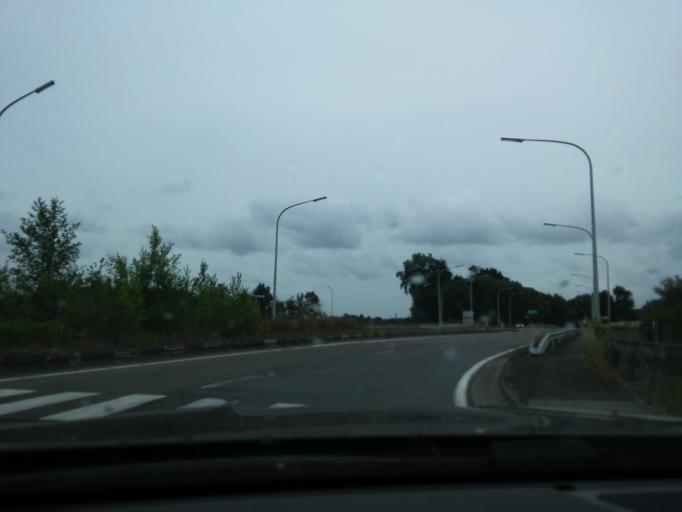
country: BE
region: Wallonia
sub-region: Province du Hainaut
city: Enghien
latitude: 50.6816
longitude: 4.0319
